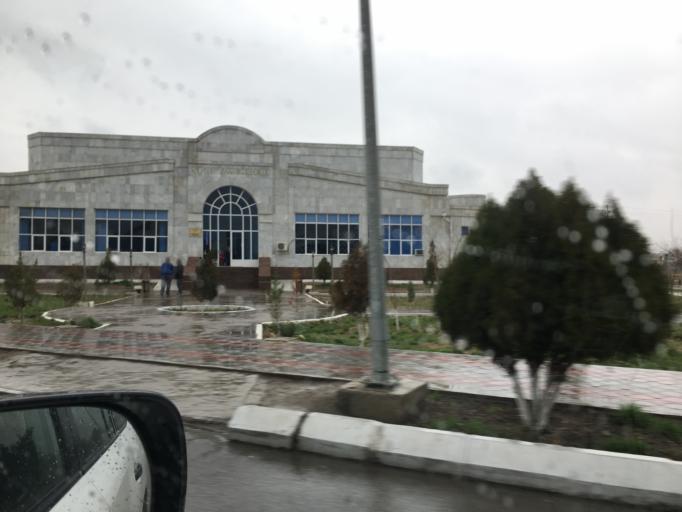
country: TM
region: Mary
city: Mary
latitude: 37.5796
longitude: 61.8347
